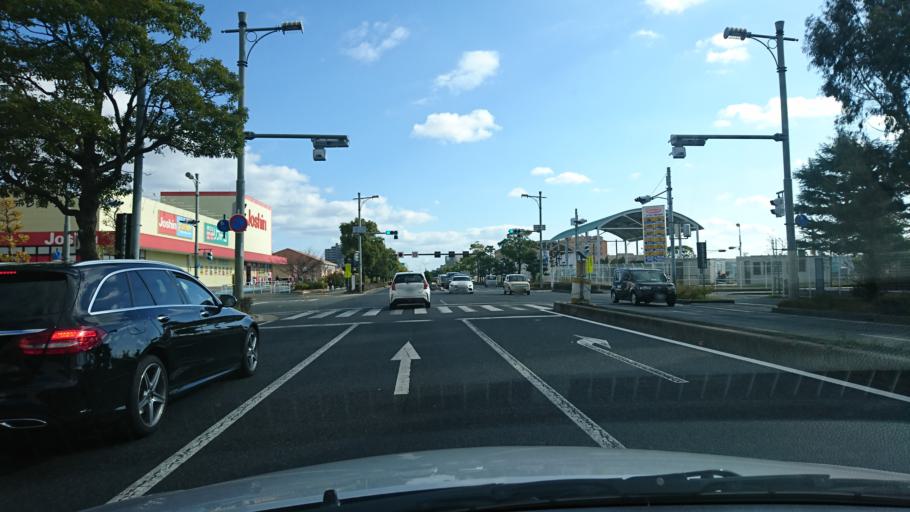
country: JP
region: Hyogo
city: Akashi
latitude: 34.6779
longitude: 134.9347
